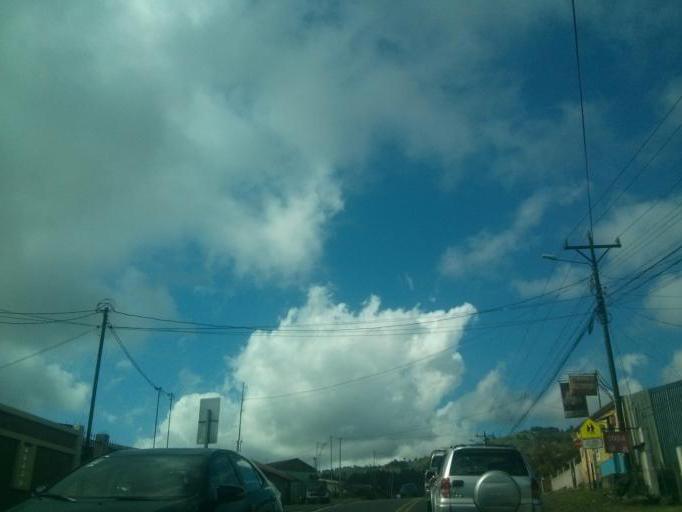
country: CR
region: Cartago
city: Cot
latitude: 9.8885
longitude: -83.8529
